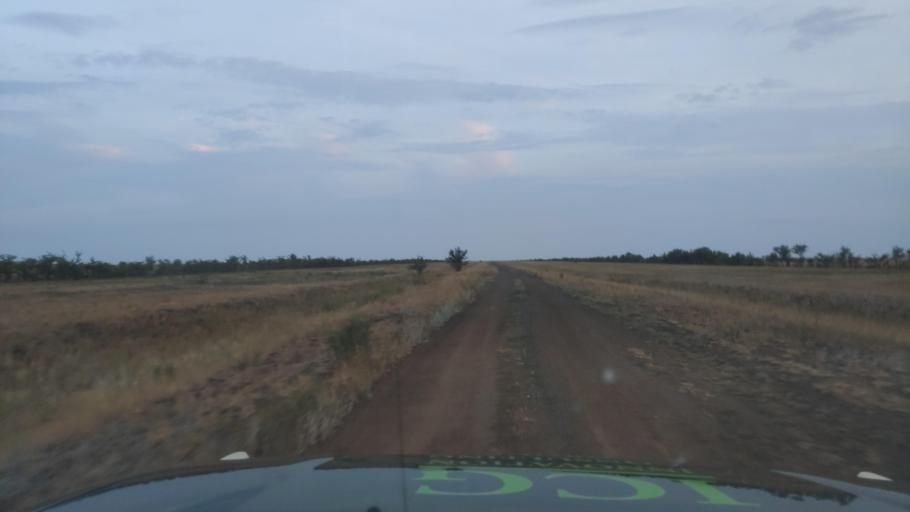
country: KZ
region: Pavlodar
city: Pavlodar
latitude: 52.1780
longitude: 77.5987
